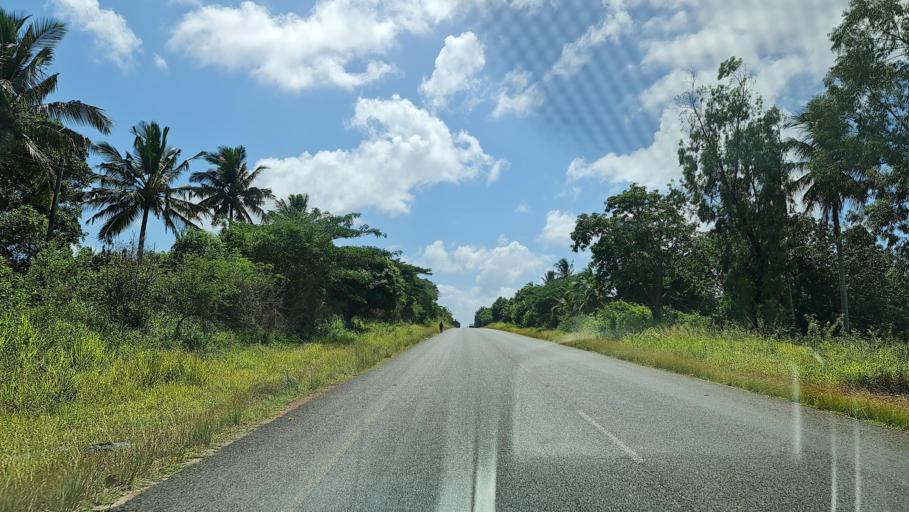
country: MZ
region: Inhambane
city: Maxixe
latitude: -24.5355
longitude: 34.9413
